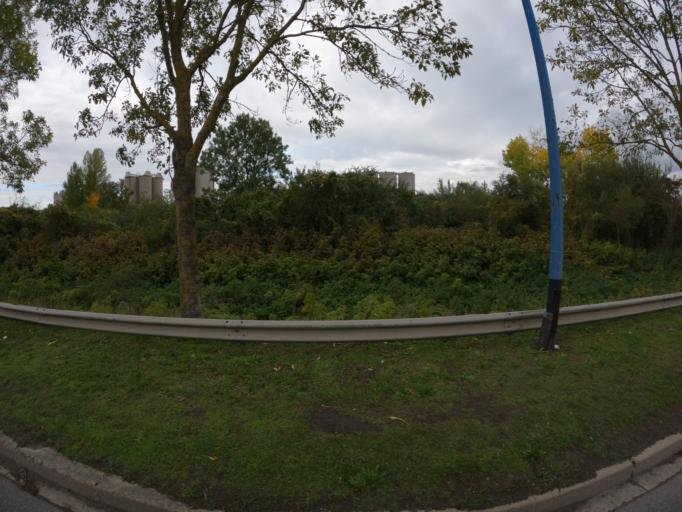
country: FR
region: Ile-de-France
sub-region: Departement de Seine-et-Marne
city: Noisiel
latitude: 48.8694
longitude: 2.6151
